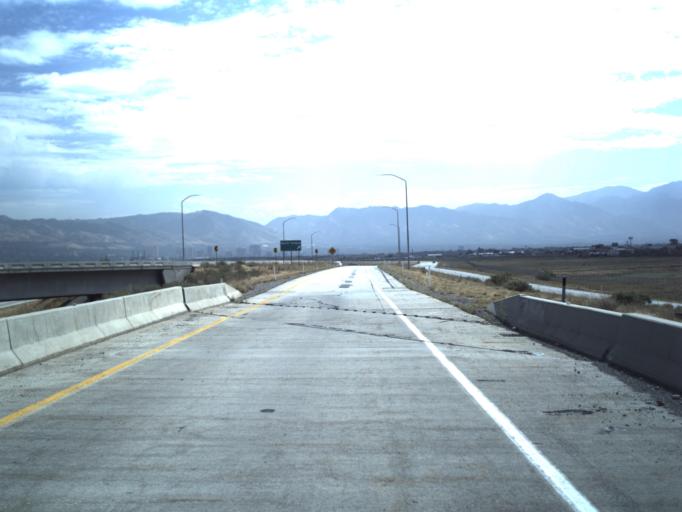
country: US
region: Utah
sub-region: Salt Lake County
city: West Valley City
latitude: 40.7637
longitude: -111.9820
